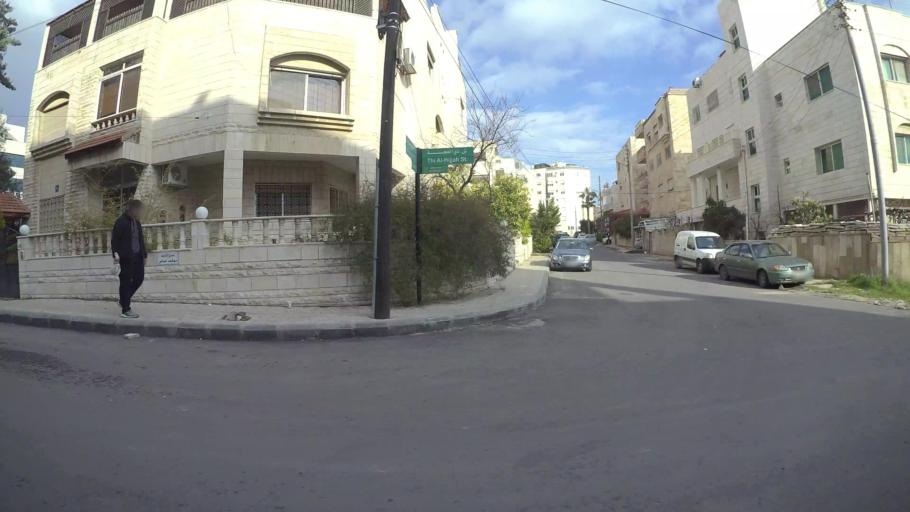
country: JO
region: Amman
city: Wadi as Sir
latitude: 31.9770
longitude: 35.8446
